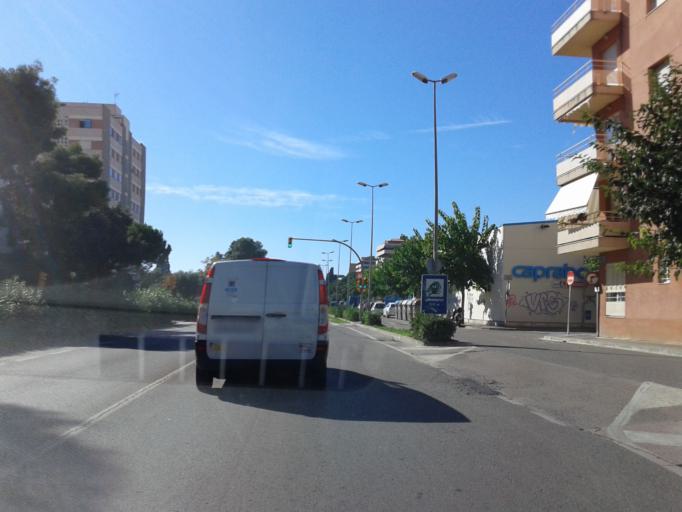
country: ES
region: Catalonia
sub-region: Provincia de Barcelona
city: Vilanova i la Geltru
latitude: 41.2193
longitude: 1.7178
